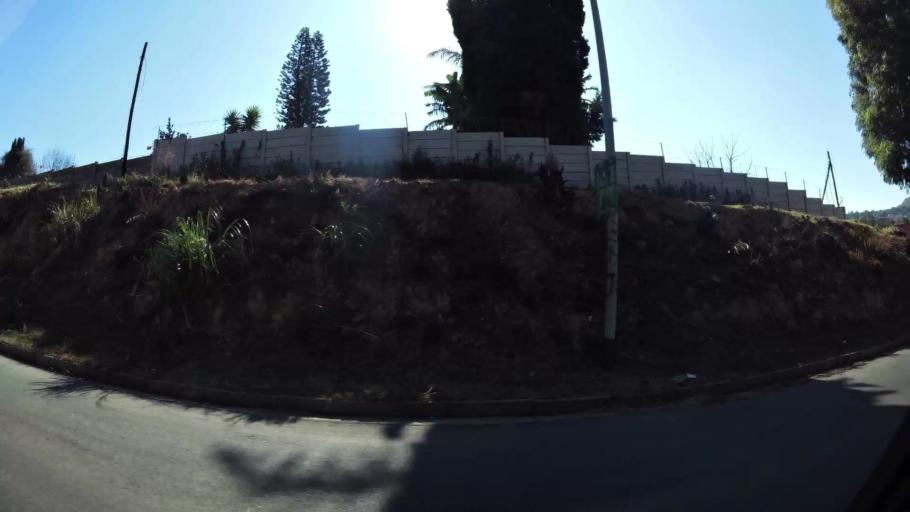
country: ZA
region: Gauteng
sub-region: City of Johannesburg Metropolitan Municipality
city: Roodepoort
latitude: -26.1241
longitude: 27.8686
